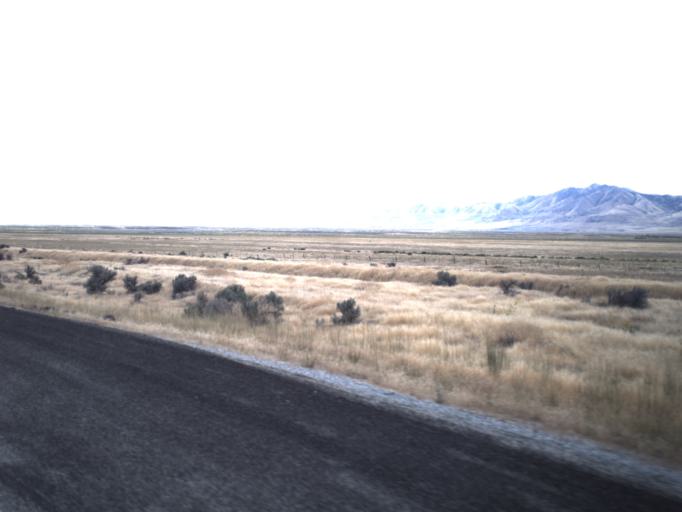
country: US
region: Utah
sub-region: Box Elder County
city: Tremonton
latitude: 41.6500
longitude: -112.4358
